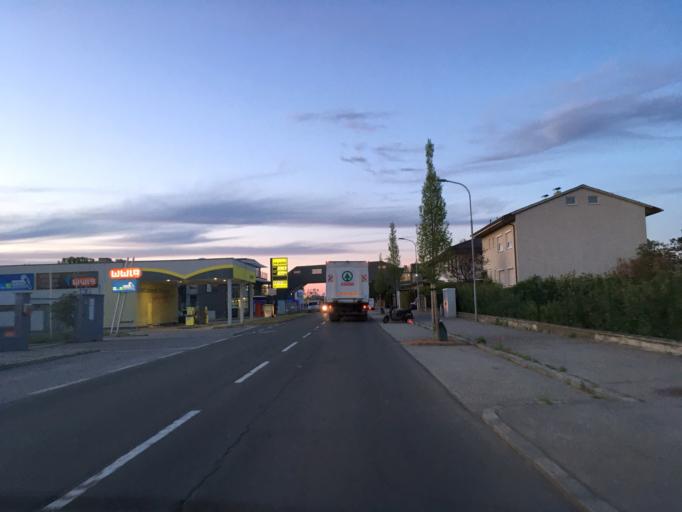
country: AT
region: Lower Austria
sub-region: Politischer Bezirk Wien-Umgebung
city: Zwolfaxing
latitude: 48.1156
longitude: 16.4664
